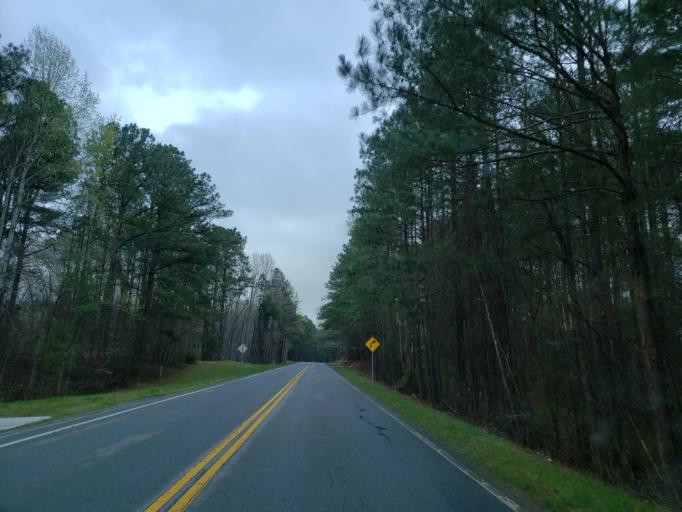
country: US
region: Georgia
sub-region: Polk County
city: Rockmart
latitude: 33.9233
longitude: -84.9611
